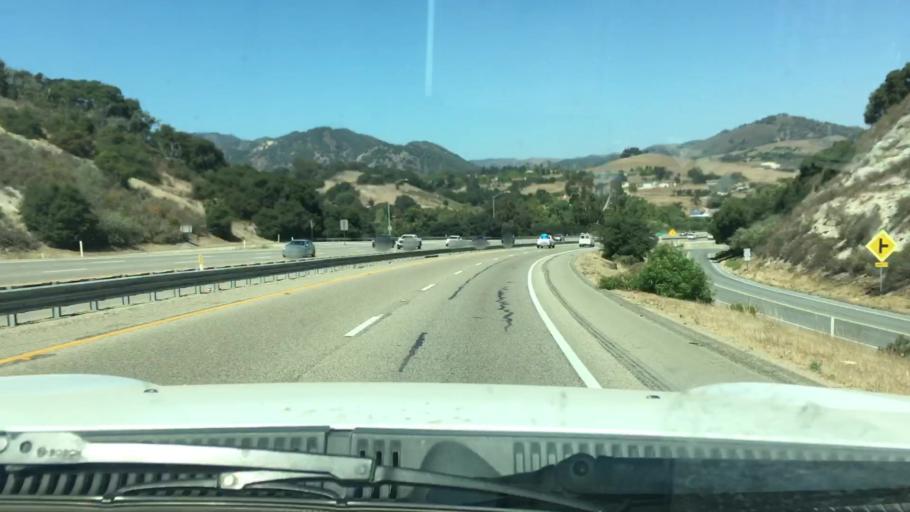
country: US
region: California
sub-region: San Luis Obispo County
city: Avila Beach
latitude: 35.1777
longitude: -120.6973
